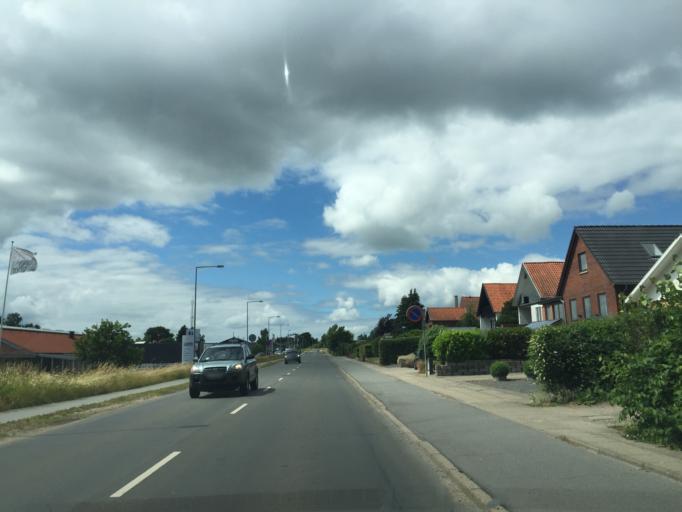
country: DK
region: South Denmark
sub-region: Svendborg Kommune
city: Svendborg
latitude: 55.0686
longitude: 10.5753
